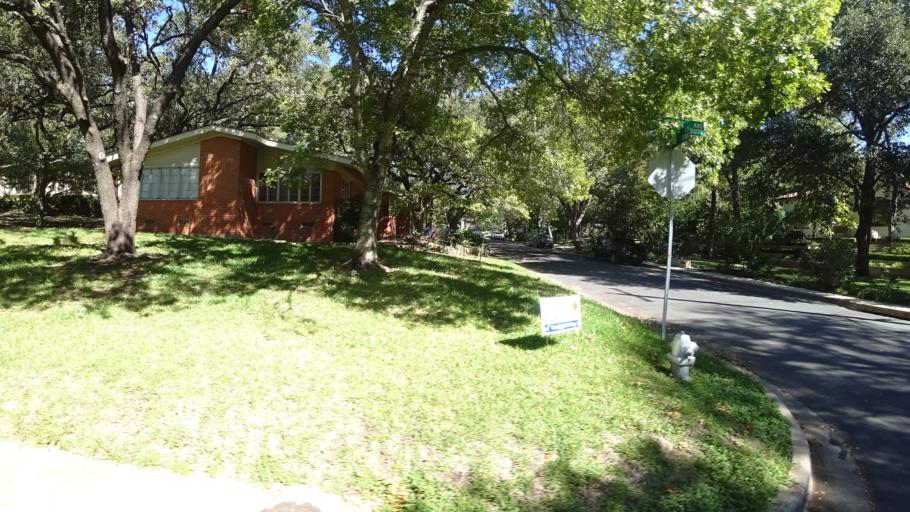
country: US
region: Texas
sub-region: Travis County
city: Rollingwood
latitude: 30.2920
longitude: -97.7694
